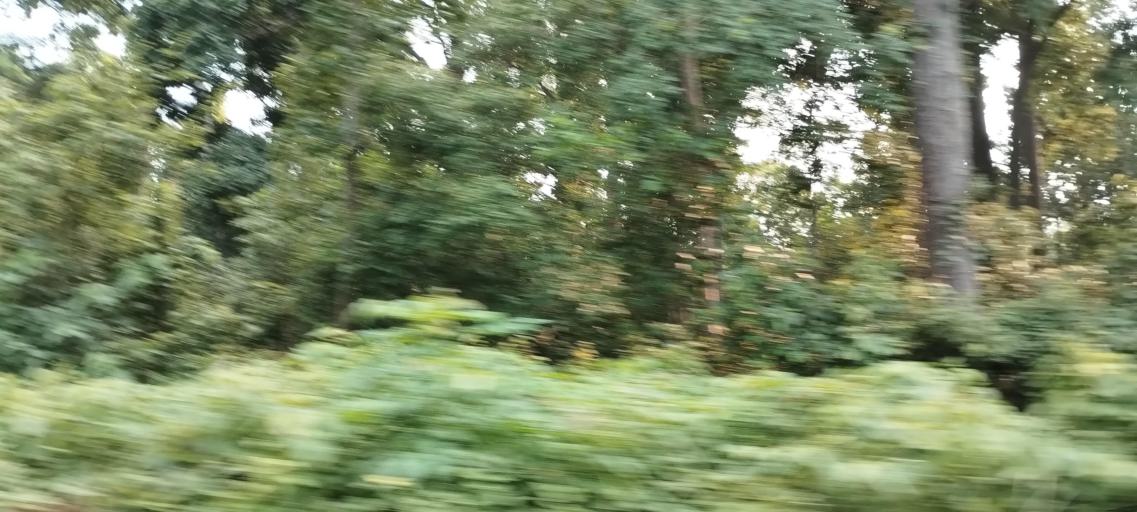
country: NP
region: Mid Western
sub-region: Bheri Zone
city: Bardiya
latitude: 28.4306
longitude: 81.3681
